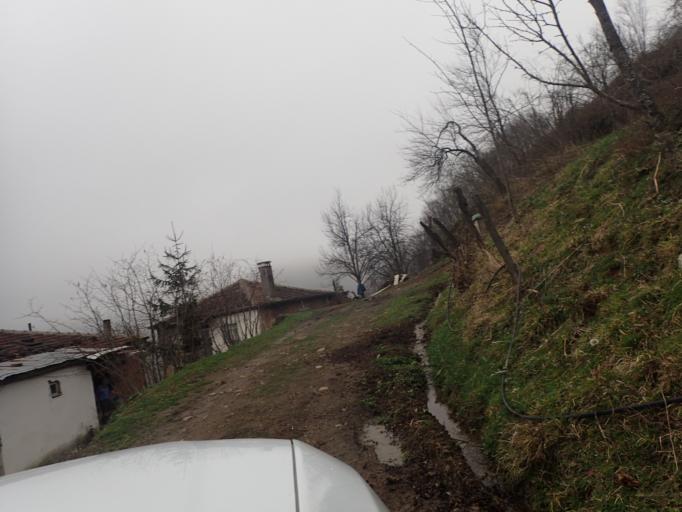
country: TR
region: Ordu
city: Camas
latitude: 40.8996
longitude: 37.5592
